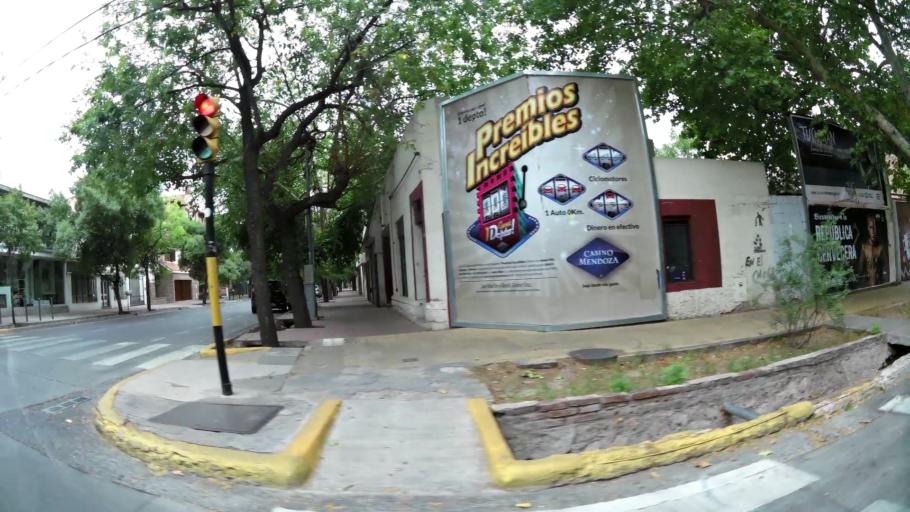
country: AR
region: Mendoza
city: Mendoza
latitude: -32.8992
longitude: -68.8417
